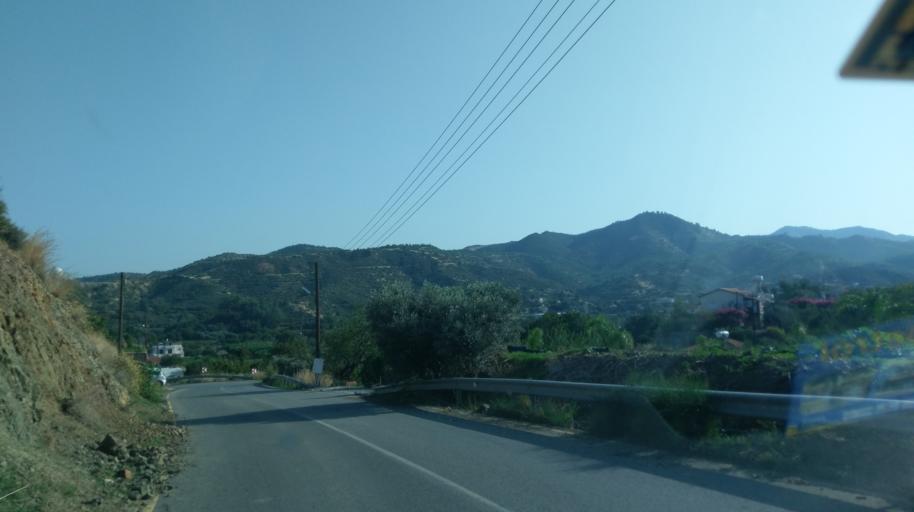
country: CY
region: Lefkosia
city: Kato Pyrgos
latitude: 35.1675
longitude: 32.7339
